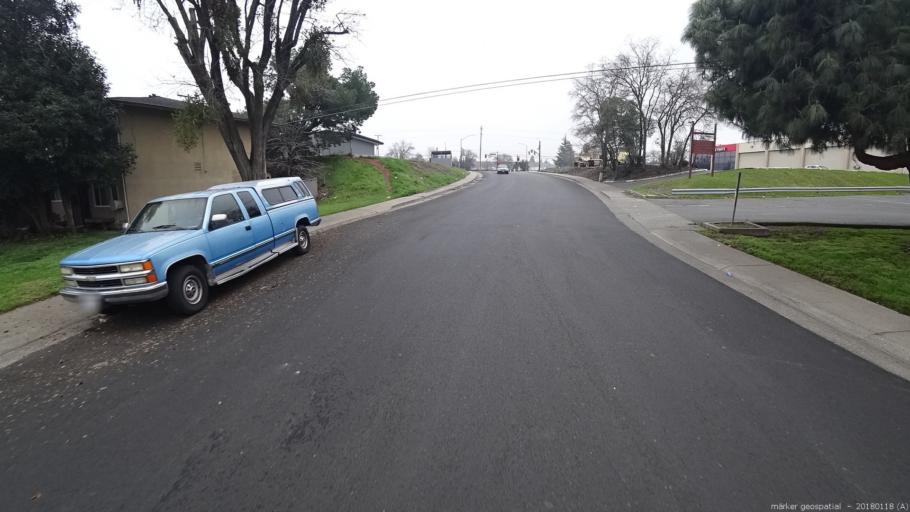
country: US
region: California
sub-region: Sacramento County
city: Rancho Cordova
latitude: 38.5838
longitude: -121.3165
